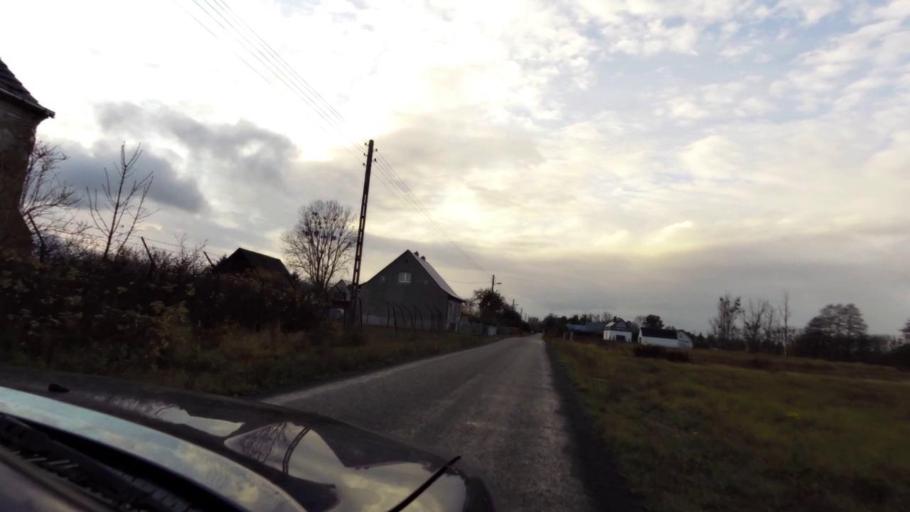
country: PL
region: West Pomeranian Voivodeship
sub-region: Powiat goleniowski
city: Goleniow
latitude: 53.5891
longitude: 14.7543
